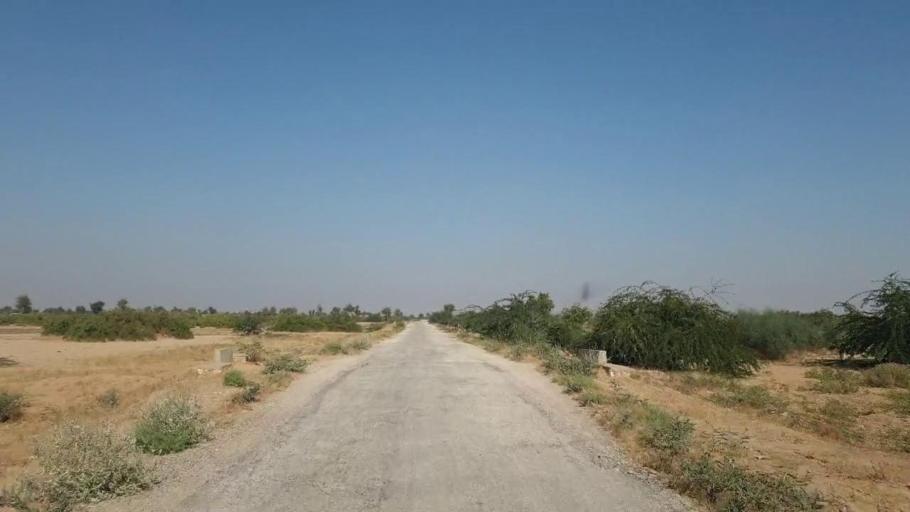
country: PK
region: Sindh
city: Jamshoro
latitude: 25.3835
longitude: 67.8455
